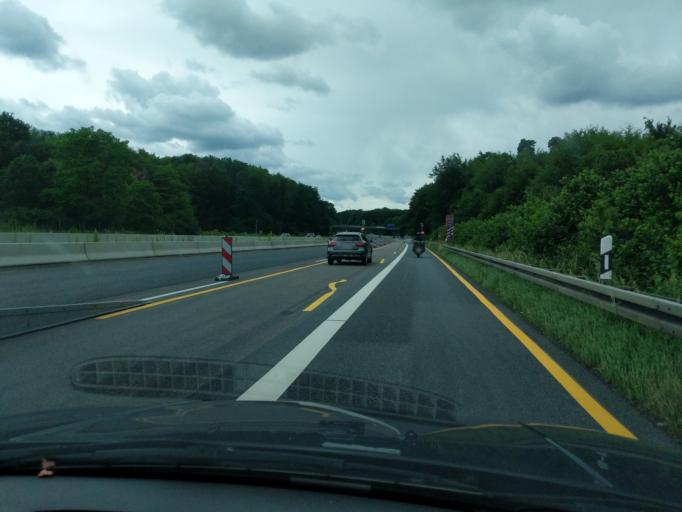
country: DE
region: Hesse
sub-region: Regierungsbezirk Darmstadt
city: Seligenstadt
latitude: 50.0319
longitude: 8.9382
